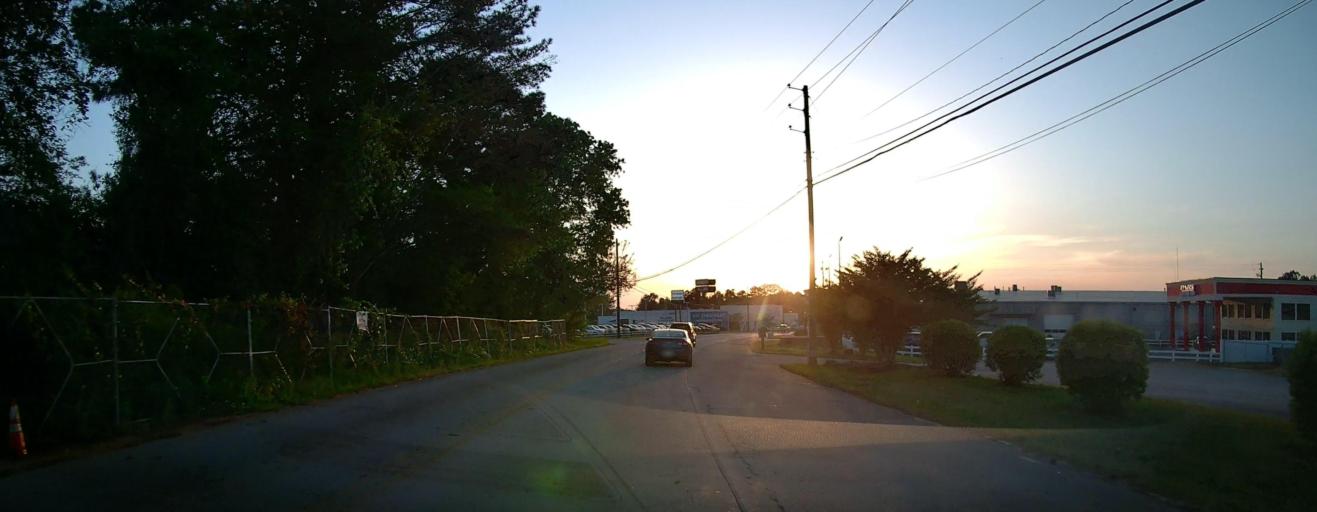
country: US
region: Georgia
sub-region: Henry County
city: McDonough
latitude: 33.4143
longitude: -84.1584
